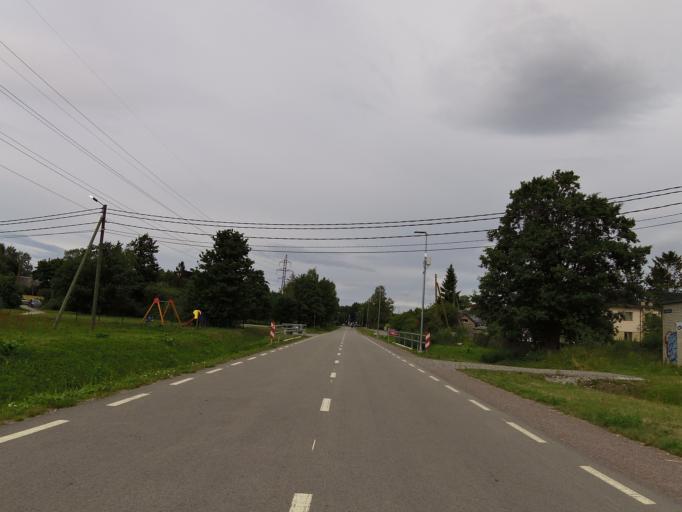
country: EE
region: Harju
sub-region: Tallinna linn
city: Tallinn
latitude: 59.4266
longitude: 24.6822
